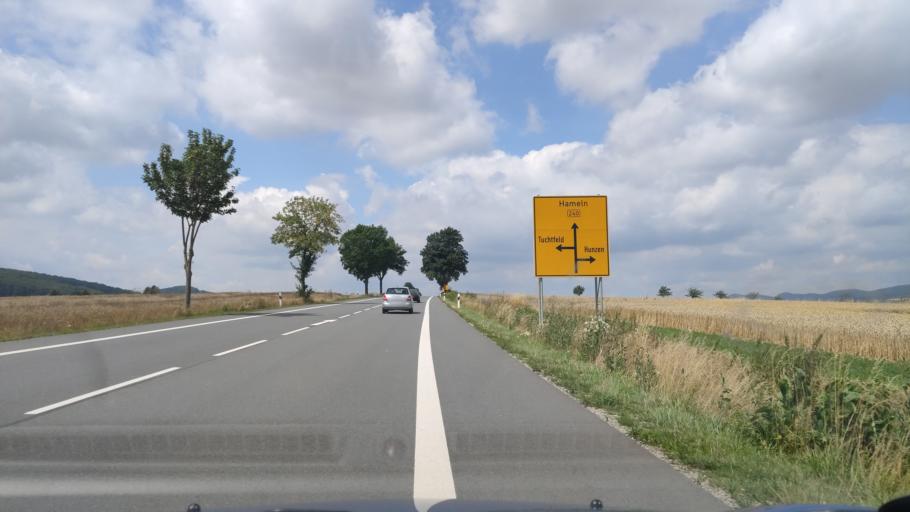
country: DE
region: Lower Saxony
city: Kirchbrak
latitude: 51.9761
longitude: 9.5837
